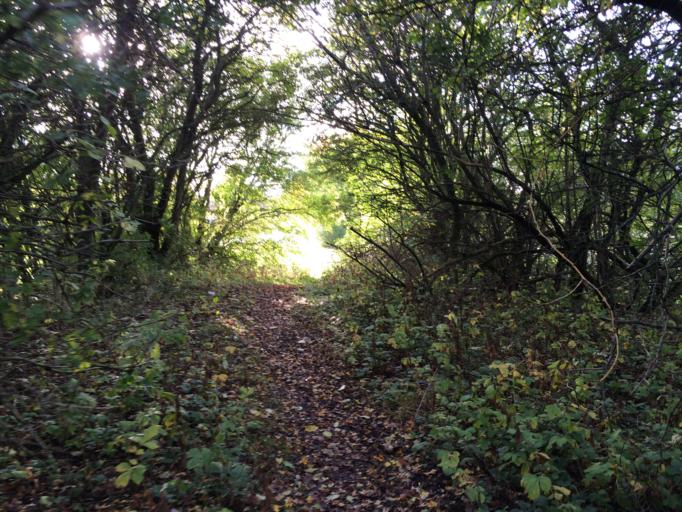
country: SE
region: Skane
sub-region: Lunds Kommun
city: Lund
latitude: 55.7275
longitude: 13.2213
